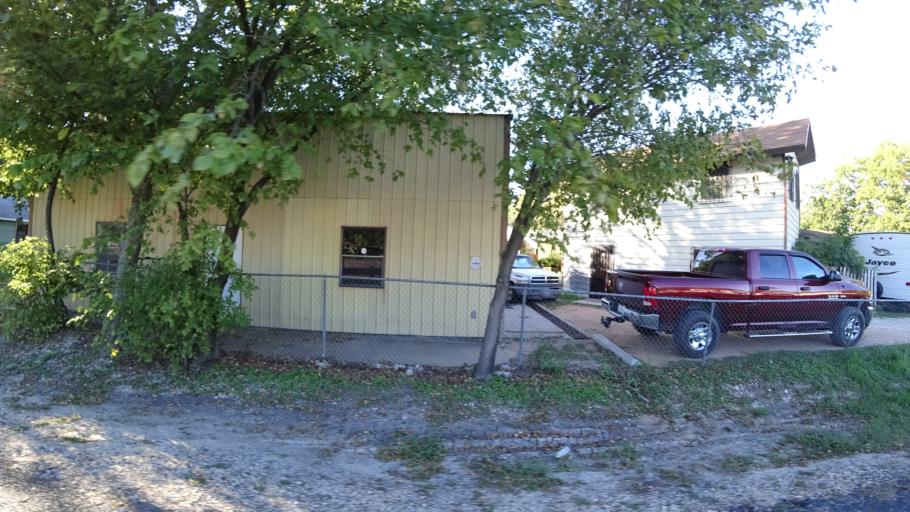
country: US
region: Texas
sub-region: Travis County
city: Austin
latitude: 30.2283
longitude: -97.6942
